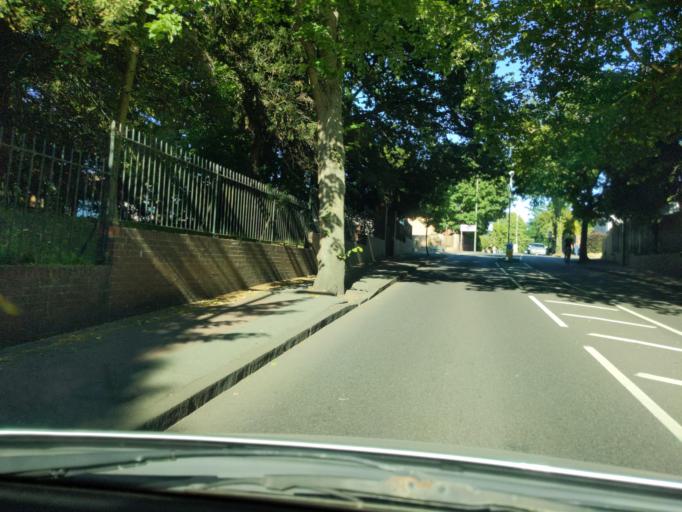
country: GB
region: England
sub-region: Greater London
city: Bromley
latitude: 51.3777
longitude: 0.0147
